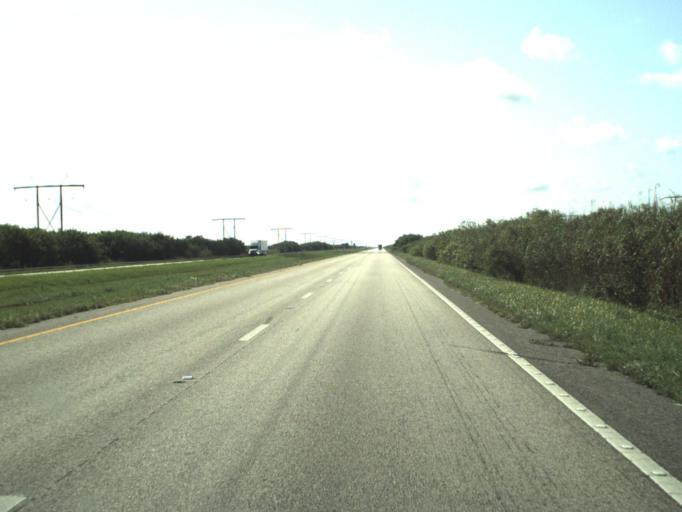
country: US
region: Florida
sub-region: Broward County
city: Weston
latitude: 26.2782
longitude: -80.4943
